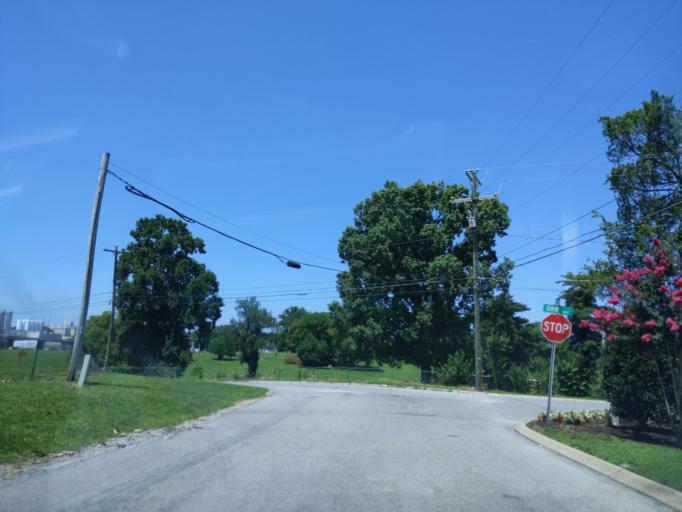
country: US
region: Tennessee
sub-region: Davidson County
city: Nashville
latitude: 36.1473
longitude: -86.7474
